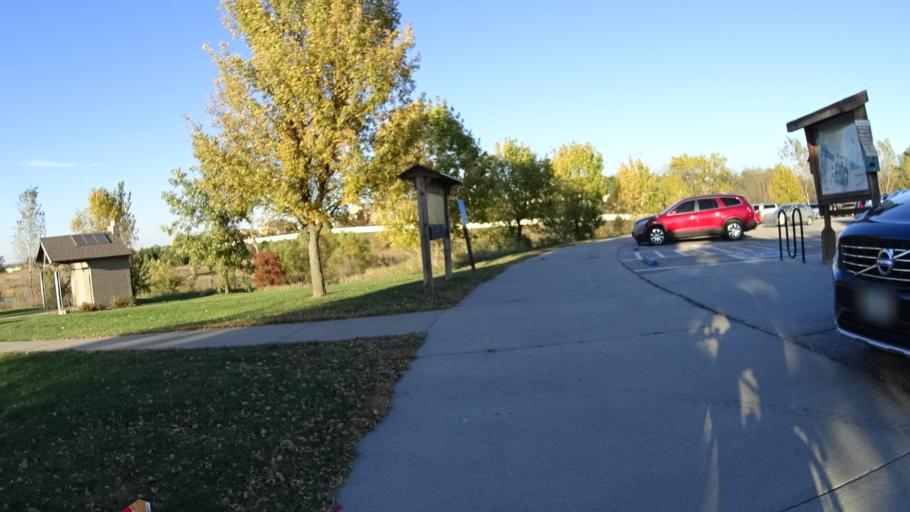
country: US
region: Nebraska
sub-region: Sarpy County
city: Papillion
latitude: 41.1401
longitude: -96.0653
